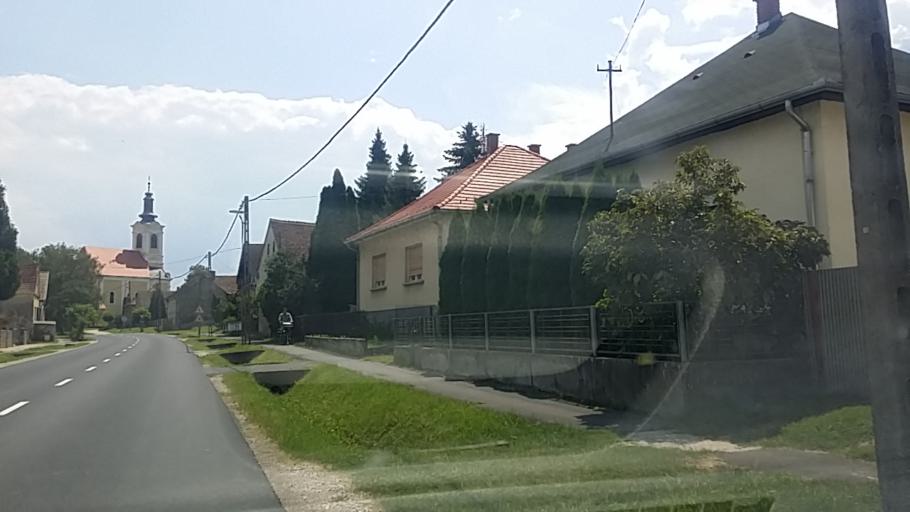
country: HR
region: Medimurska
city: Podturen
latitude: 46.5229
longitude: 16.5552
